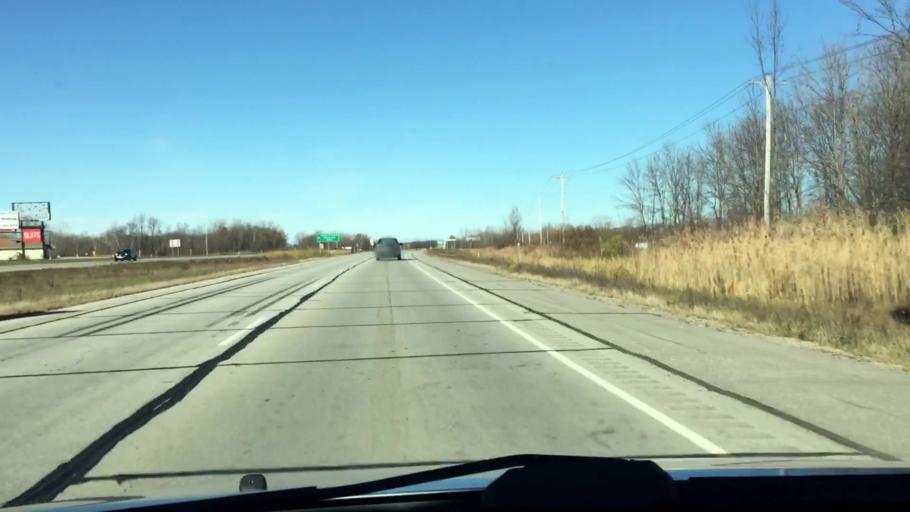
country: US
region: Wisconsin
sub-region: Brown County
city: Oneida
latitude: 44.5823
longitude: -88.1860
